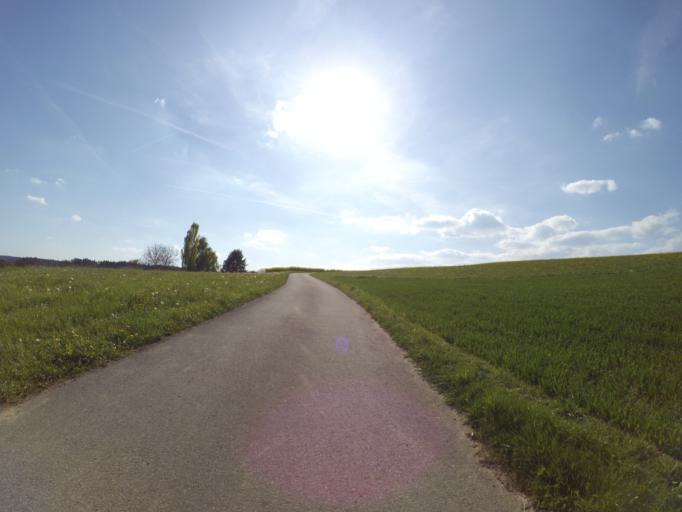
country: CH
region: Thurgau
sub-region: Frauenfeld District
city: Diessenhofen
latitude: 47.6606
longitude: 8.7656
